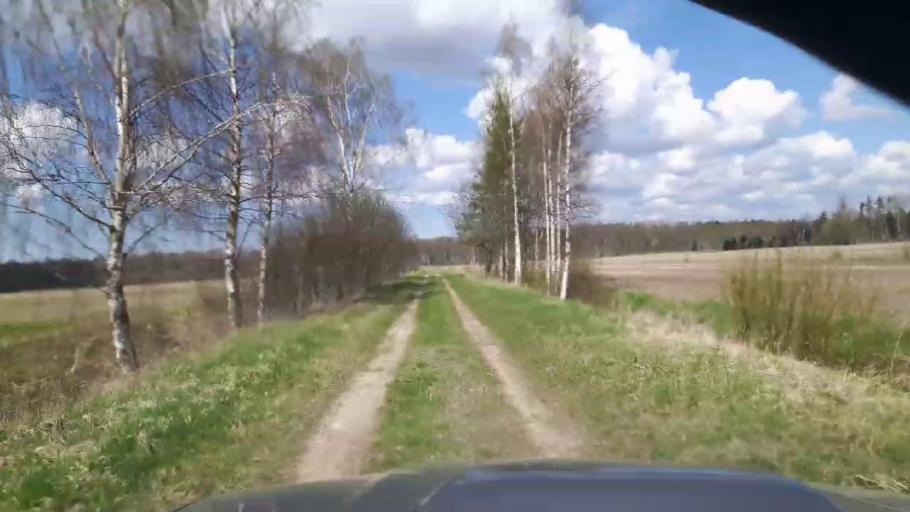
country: EE
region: Paernumaa
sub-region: Vaendra vald (alev)
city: Vandra
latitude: 58.5436
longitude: 25.0783
